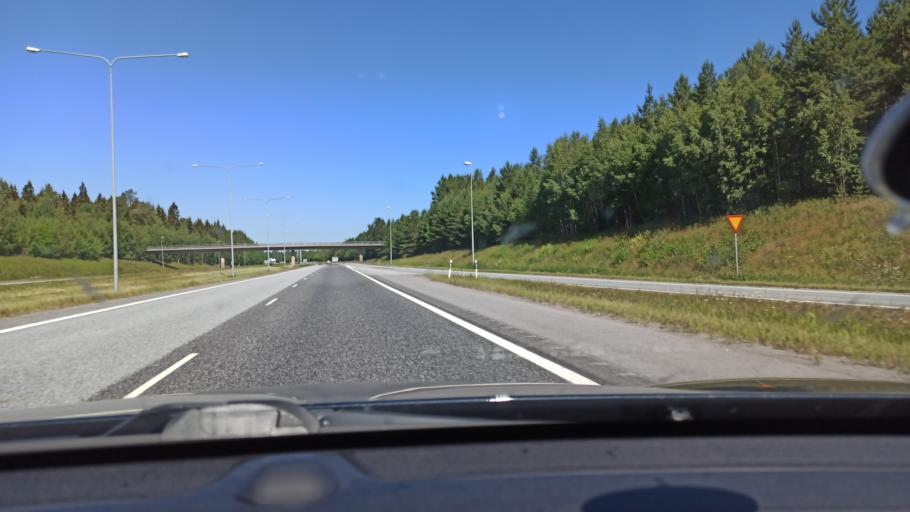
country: FI
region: Ostrobothnia
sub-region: Vaasa
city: Ristinummi
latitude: 63.0561
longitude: 21.7128
